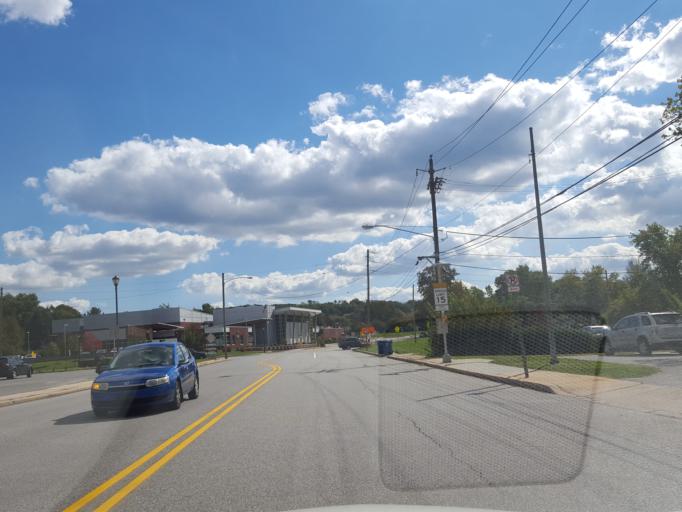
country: US
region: Pennsylvania
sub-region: York County
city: East York
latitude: 39.9762
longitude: -76.6673
